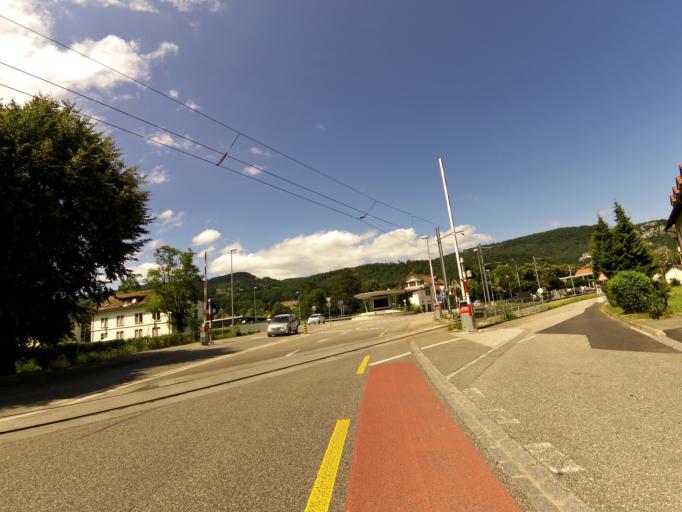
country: CH
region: Solothurn
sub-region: Bezirk Thal
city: Balsthal
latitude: 47.3090
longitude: 7.6884
